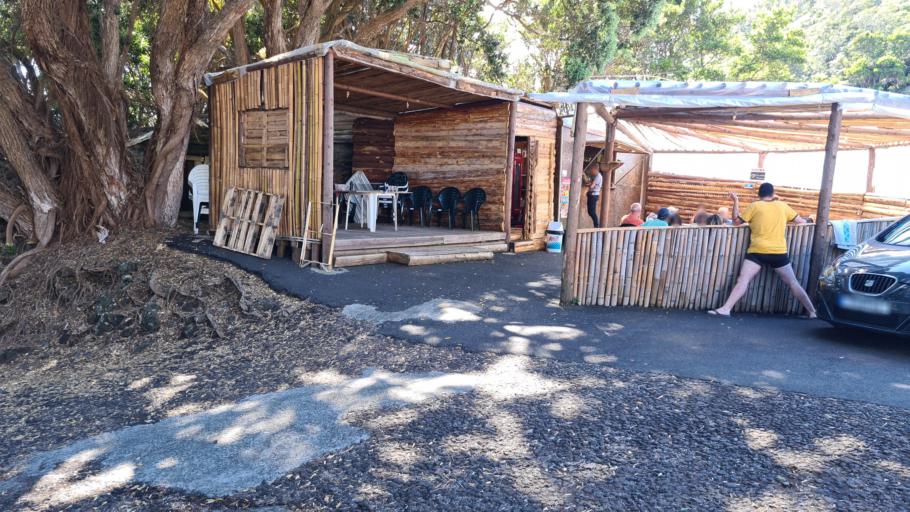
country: PT
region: Azores
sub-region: Sao Roque do Pico
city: Sao Roque do Pico
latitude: 38.4130
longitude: -28.2891
